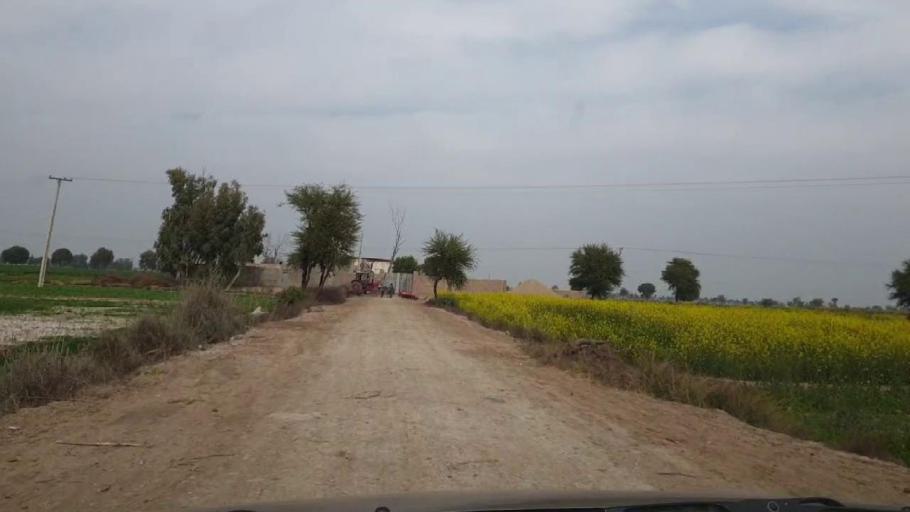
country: PK
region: Sindh
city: Sinjhoro
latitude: 26.0725
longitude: 68.8324
